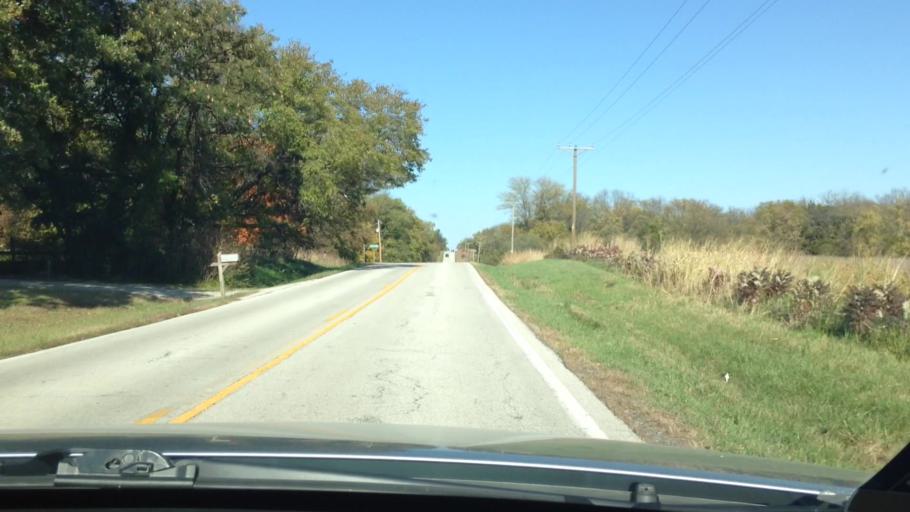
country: US
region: Missouri
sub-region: Platte County
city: Weatherby Lake
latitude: 39.3167
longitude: -94.6488
